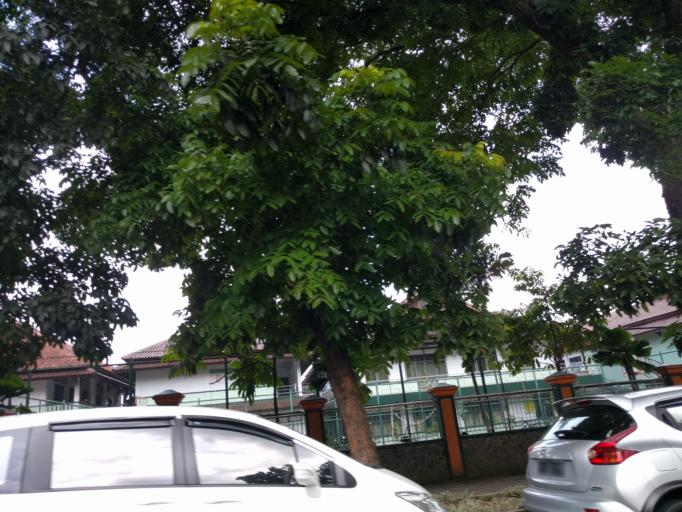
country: ID
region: West Java
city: Bogor
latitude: -6.6064
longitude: 106.8084
